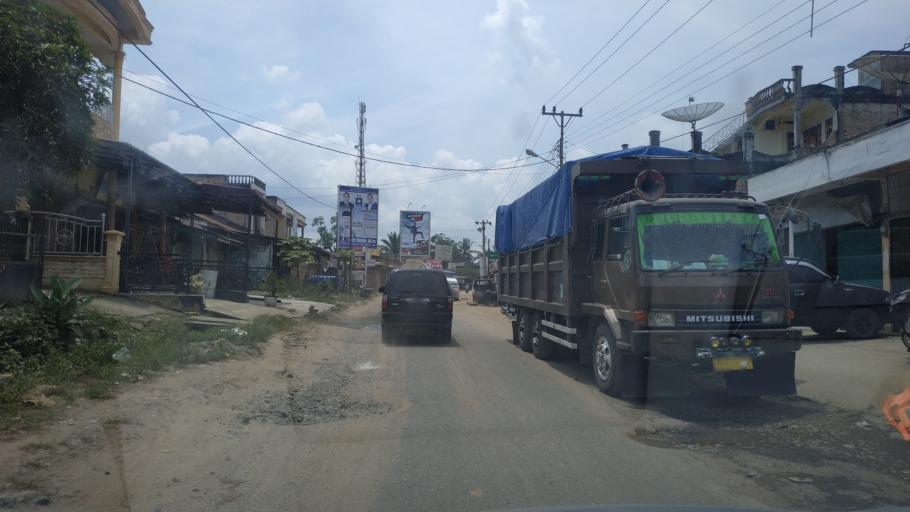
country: ID
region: North Sumatra
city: Langgapayung
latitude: 1.7279
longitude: 99.9611
